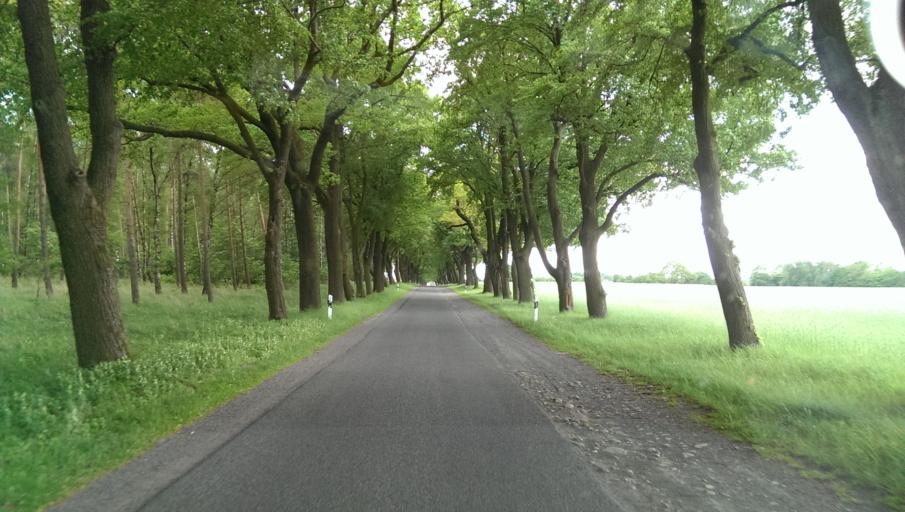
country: DE
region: Brandenburg
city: Wiesenburg
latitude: 52.1485
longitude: 12.4816
